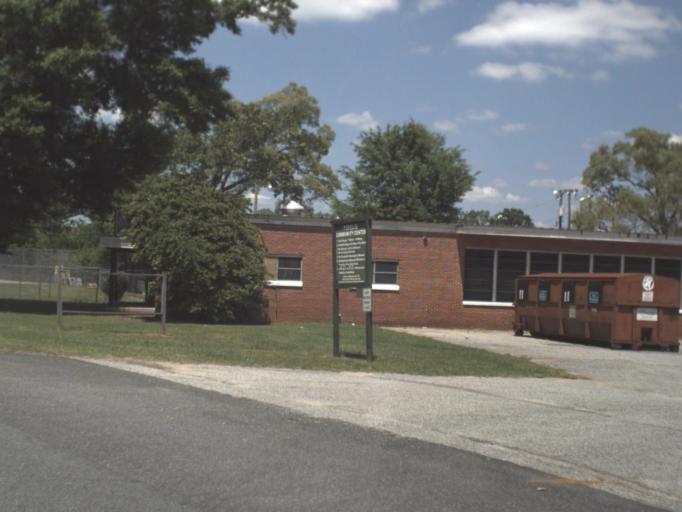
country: US
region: Alabama
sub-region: Escambia County
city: East Brewton
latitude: 30.9347
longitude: -87.0232
